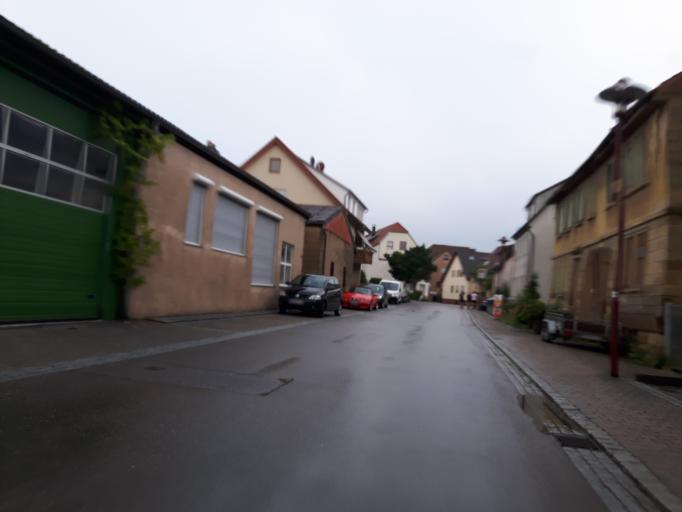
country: DE
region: Baden-Wuerttemberg
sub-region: Regierungsbezirk Stuttgart
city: Erlenbach
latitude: 49.1709
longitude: 9.2665
